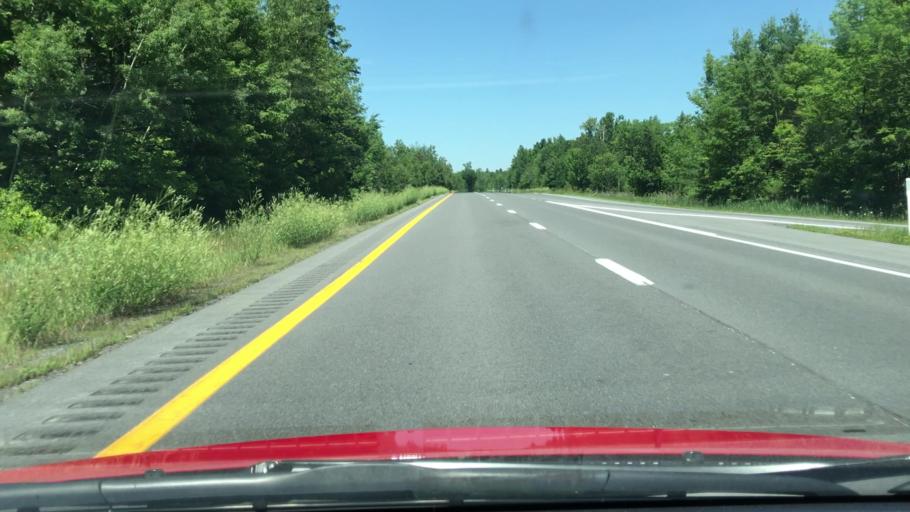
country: US
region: New York
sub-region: Clinton County
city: Champlain
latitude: 44.8915
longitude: -73.4535
